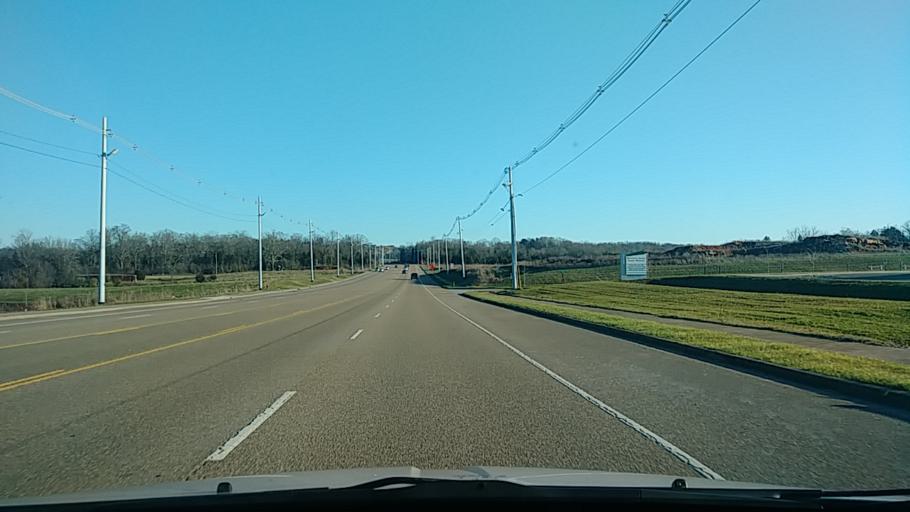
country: US
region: Tennessee
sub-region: Hamblen County
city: Morristown
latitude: 36.1862
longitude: -83.3564
